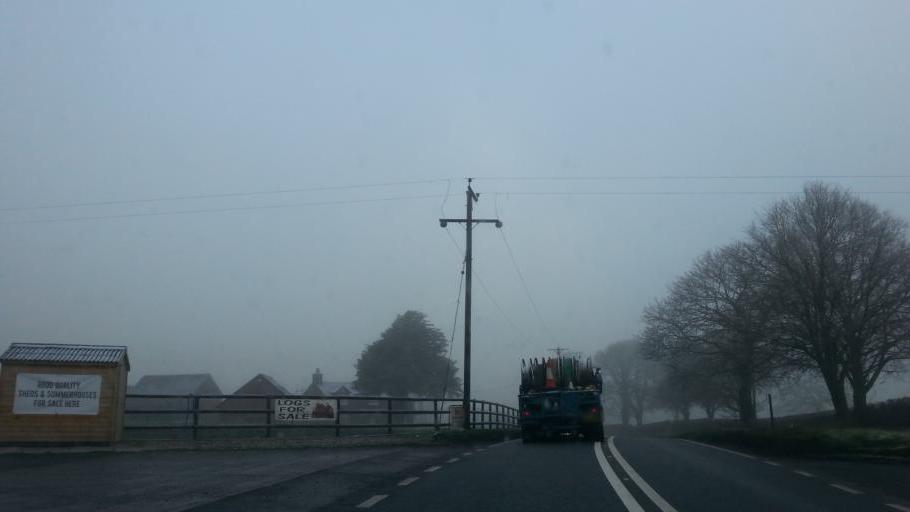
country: GB
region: England
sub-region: Cheshire East
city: Siddington
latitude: 53.2186
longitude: -2.2360
